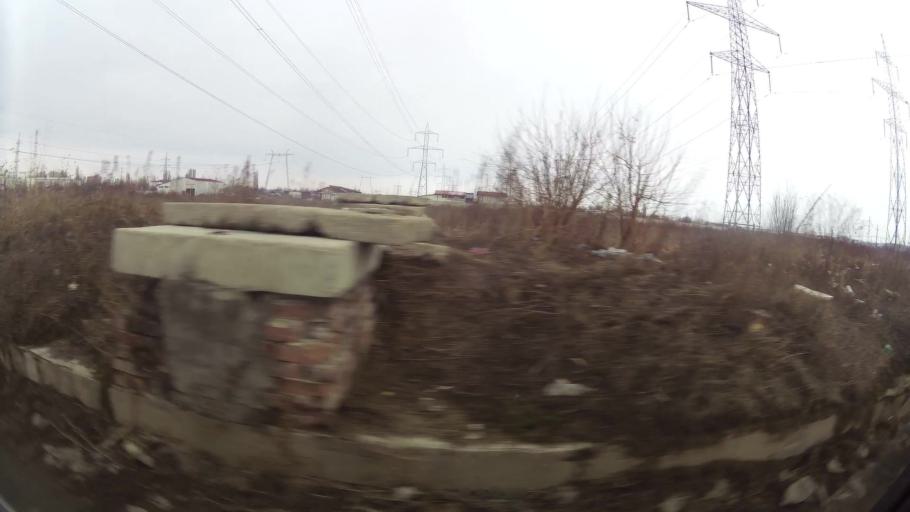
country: RO
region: Ilfov
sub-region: Comuna Glina
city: Catelu
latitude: 44.3966
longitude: 26.2020
